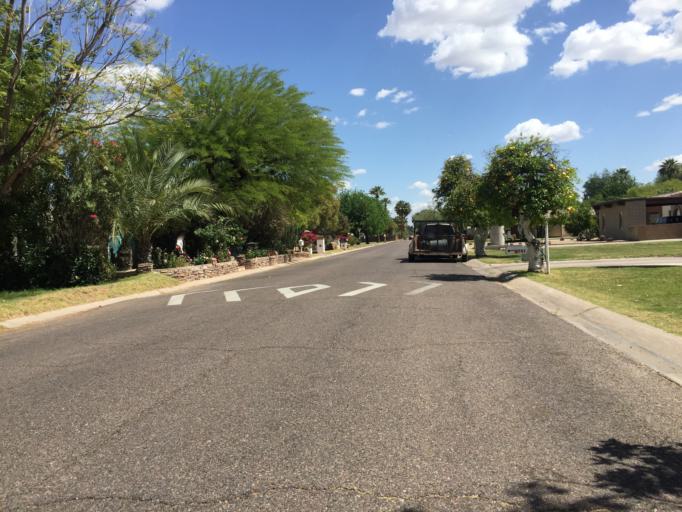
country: US
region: Arizona
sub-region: Maricopa County
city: Phoenix
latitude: 33.5328
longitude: -112.0633
